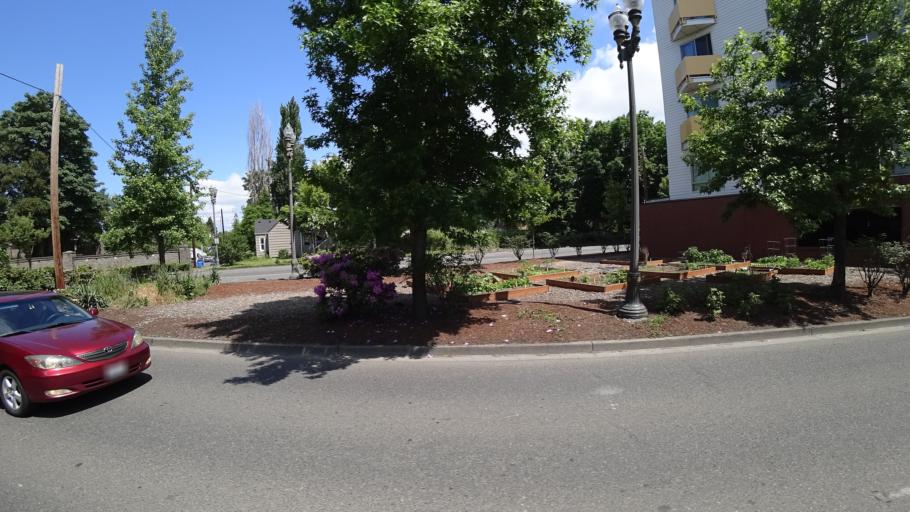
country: US
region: Washington
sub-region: Clark County
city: Vancouver
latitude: 45.6324
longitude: -122.6758
